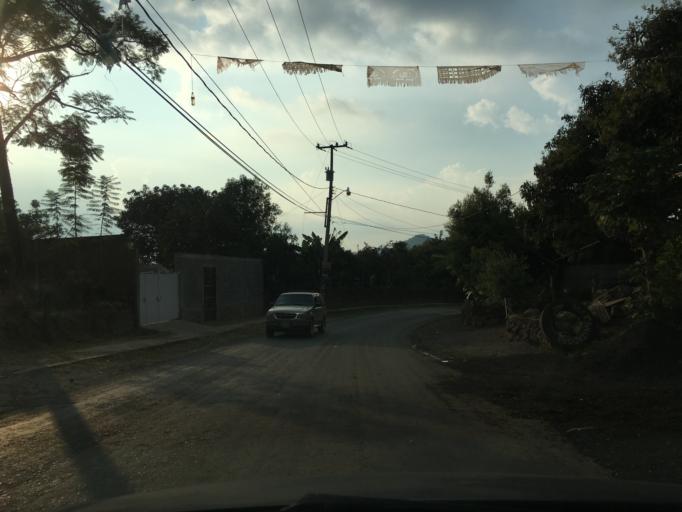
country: MX
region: Michoacan
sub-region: Ziracuaretiro
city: Patuan
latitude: 19.4443
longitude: -101.8871
